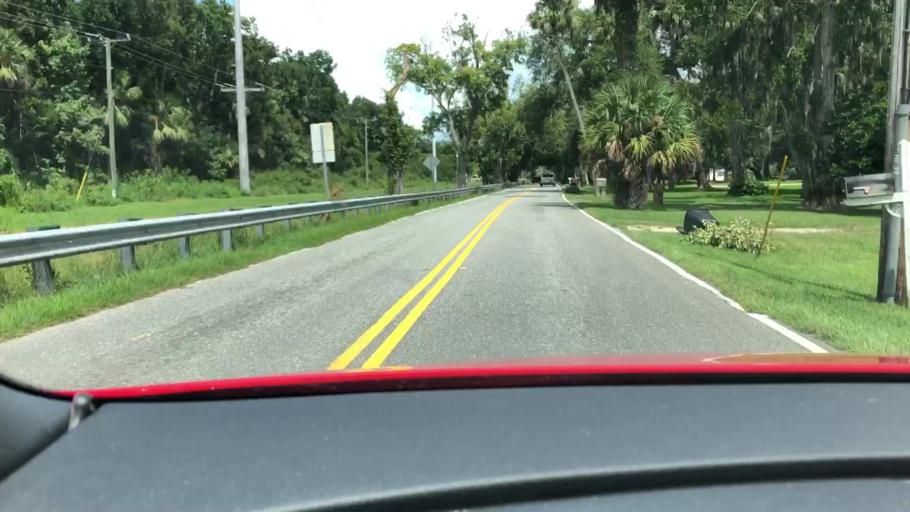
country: US
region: Florida
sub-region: Volusia County
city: Port Orange
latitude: 29.1370
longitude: -81.0078
